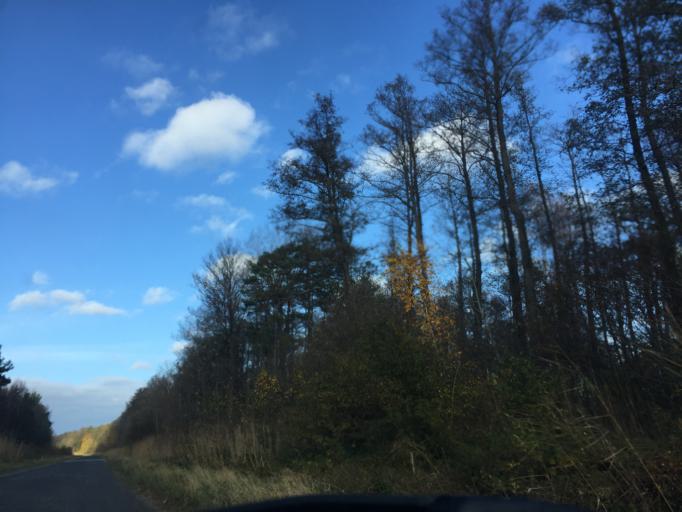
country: LV
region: Liepaja
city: Vec-Liepaja
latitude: 56.5683
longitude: 21.0526
